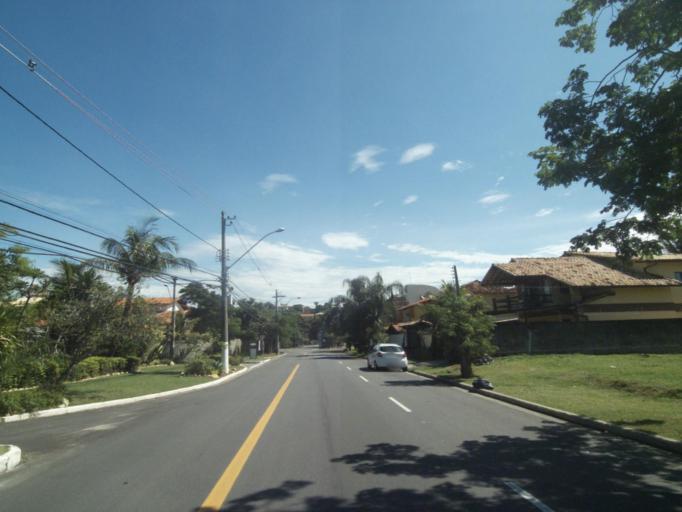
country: BR
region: Rio de Janeiro
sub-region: Niteroi
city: Niteroi
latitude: -22.9547
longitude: -43.0583
